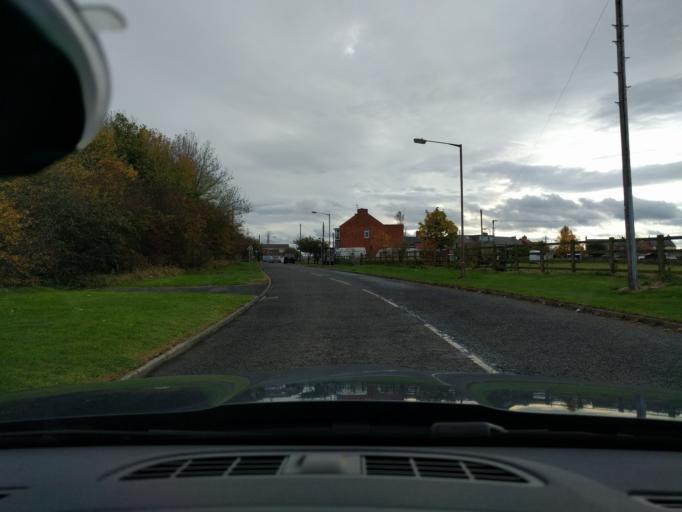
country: GB
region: England
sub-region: Northumberland
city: Ashington
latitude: 55.1461
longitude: -1.5496
